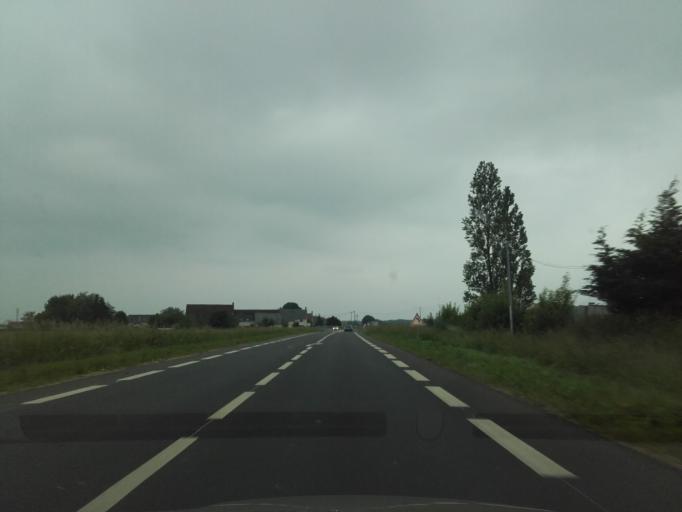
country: FR
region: Centre
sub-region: Departement d'Indre-et-Loire
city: Chanceaux-sur-Choisille
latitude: 47.4636
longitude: 0.6929
